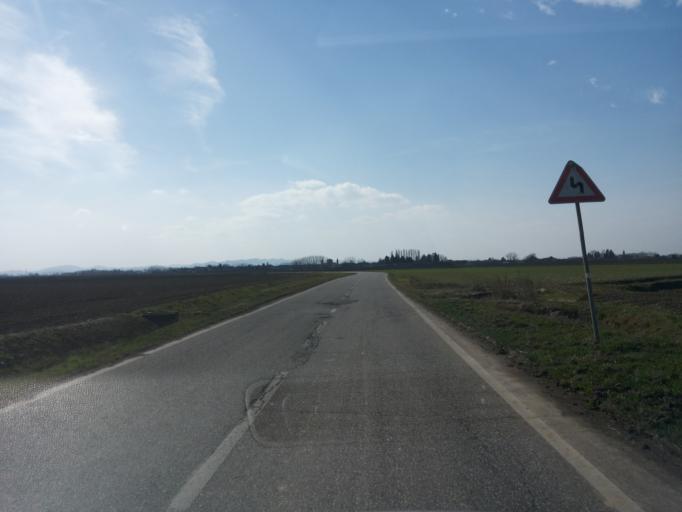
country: IT
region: Piedmont
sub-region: Provincia di Vercelli
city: Costanzana
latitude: 45.2441
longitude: 8.3835
